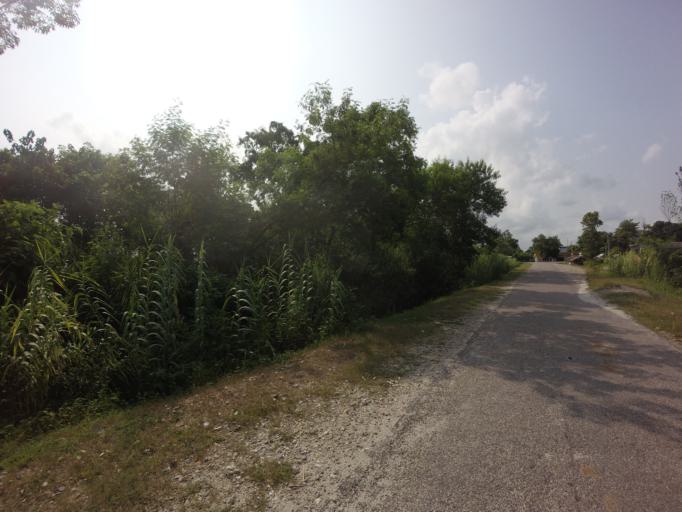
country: NP
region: Far Western
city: Tikapur
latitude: 28.4708
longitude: 81.0710
